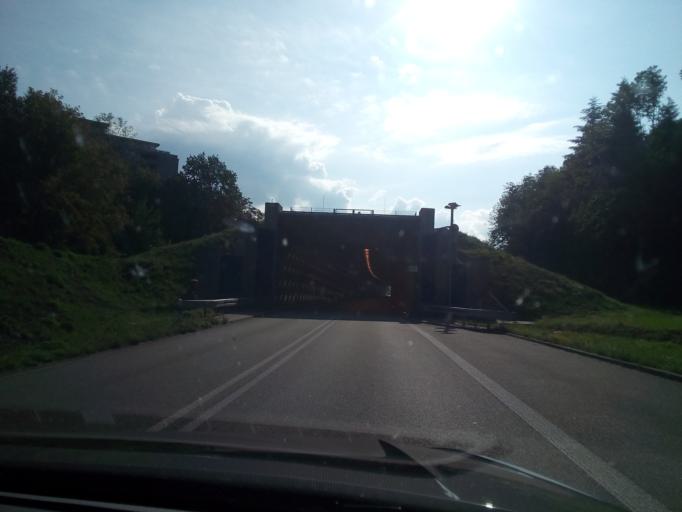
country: DE
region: Baden-Wuerttemberg
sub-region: Freiburg Region
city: Oberkirch
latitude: 48.5220
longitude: 8.0802
